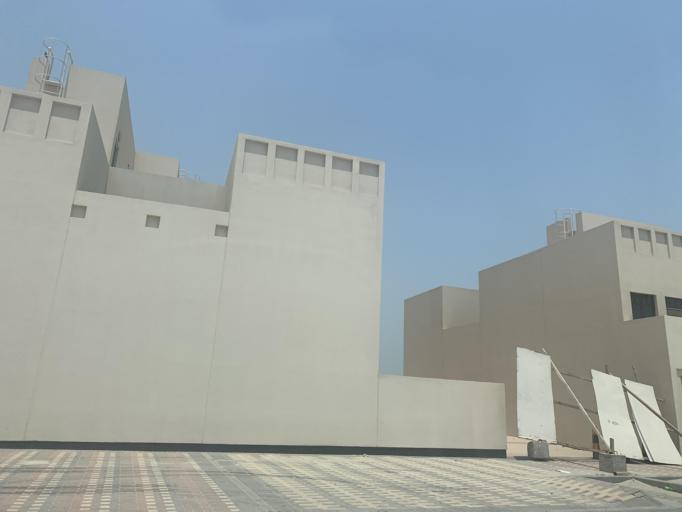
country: BH
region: Muharraq
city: Al Hadd
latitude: 26.2412
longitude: 50.6719
